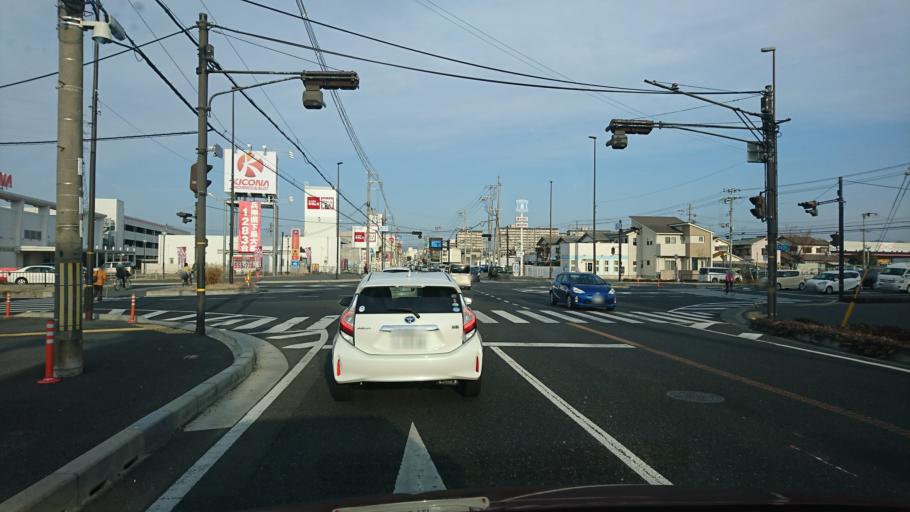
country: JP
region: Hyogo
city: Kakogawacho-honmachi
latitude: 34.7562
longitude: 134.8493
